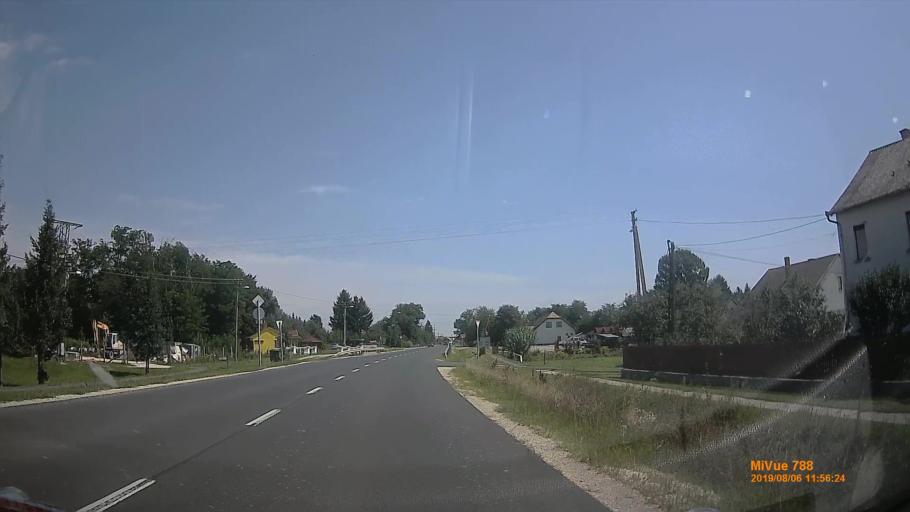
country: HU
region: Vas
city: Kormend
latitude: 47.0559
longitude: 16.6964
